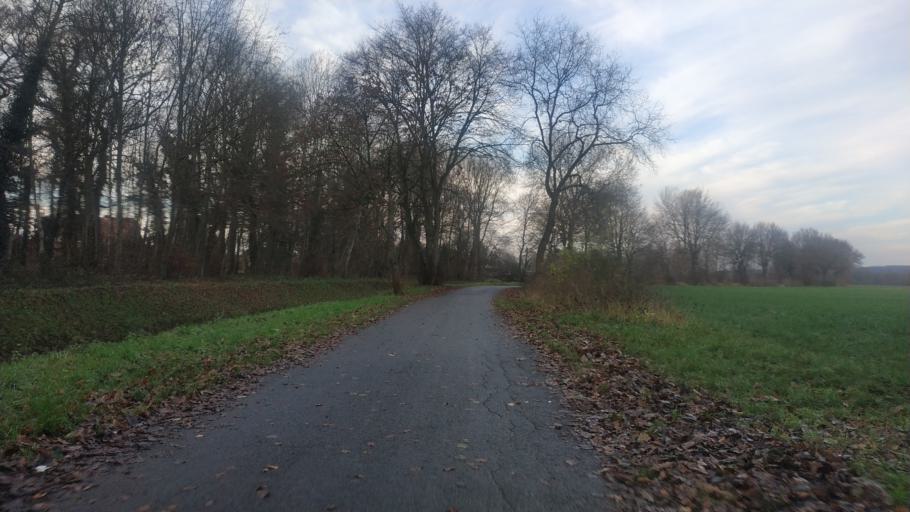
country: DE
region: North Rhine-Westphalia
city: Ibbenburen
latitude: 52.2770
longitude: 7.6873
